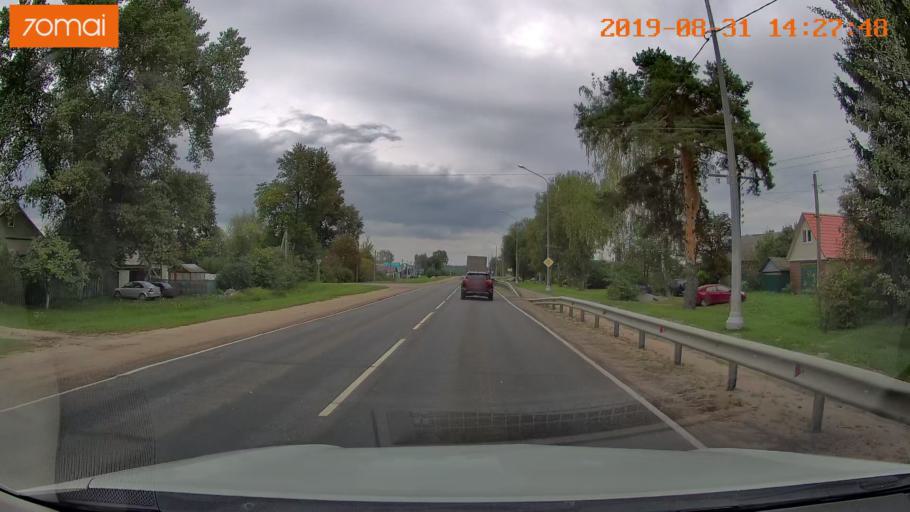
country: RU
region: Smolensk
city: Yekimovichi
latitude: 54.1177
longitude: 33.3046
